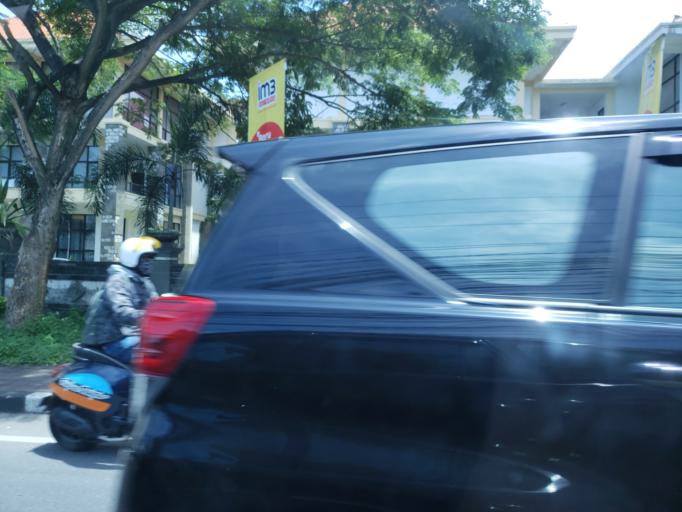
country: ID
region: Bali
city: Jimbaran
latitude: -8.7986
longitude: 115.1608
